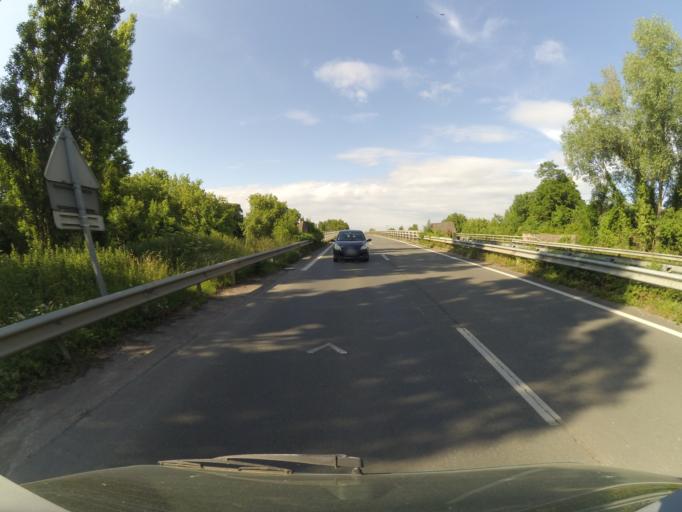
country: FR
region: Poitou-Charentes
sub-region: Departement de la Charente-Maritime
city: Saint-Agnant
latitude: 45.8737
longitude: -0.9680
